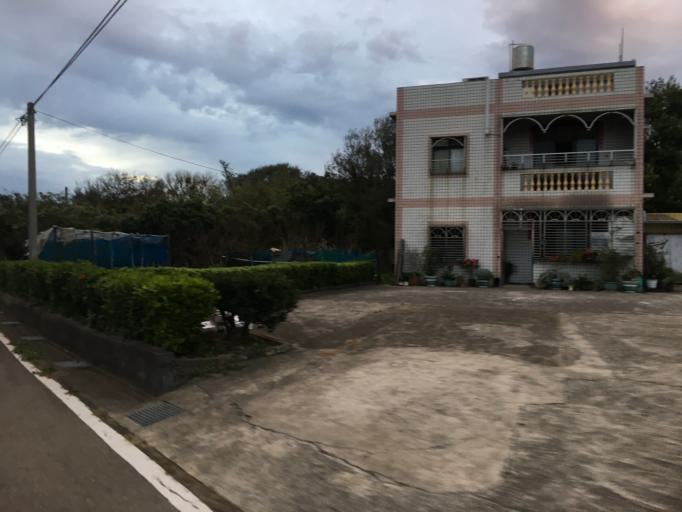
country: TW
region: Taiwan
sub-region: Hsinchu
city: Hsinchu
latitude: 24.7292
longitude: 120.8769
